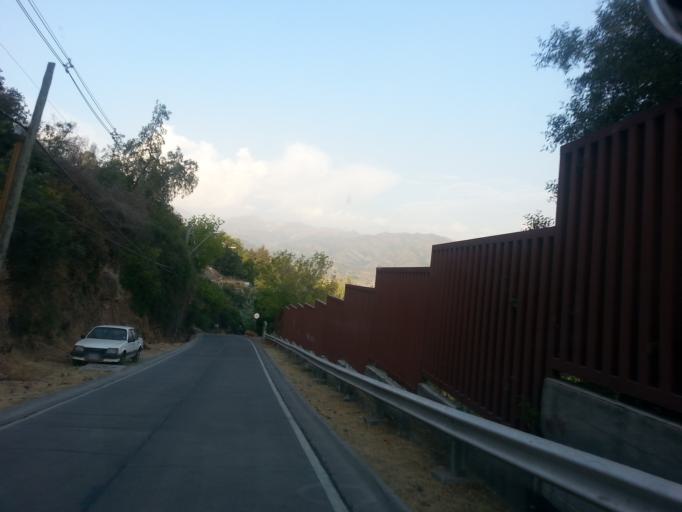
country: CL
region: Santiago Metropolitan
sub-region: Provincia de Santiago
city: Villa Presidente Frei, Nunoa, Santiago, Chile
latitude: -33.3640
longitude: -70.5571
